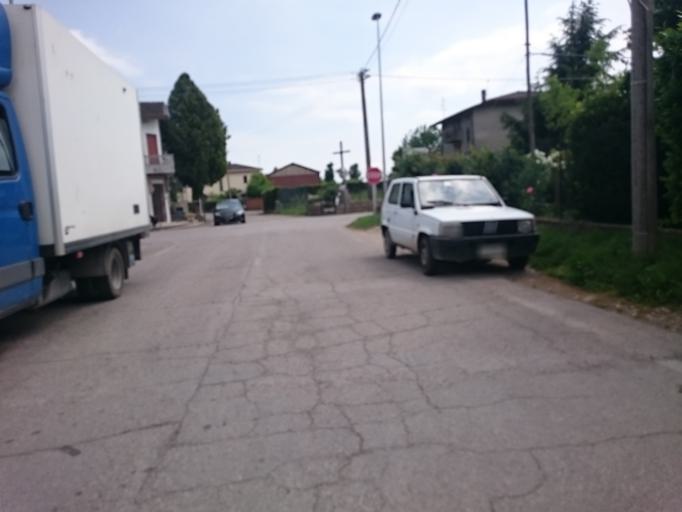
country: IT
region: Veneto
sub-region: Provincia di Padova
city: Carceri
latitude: 45.1908
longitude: 11.6156
